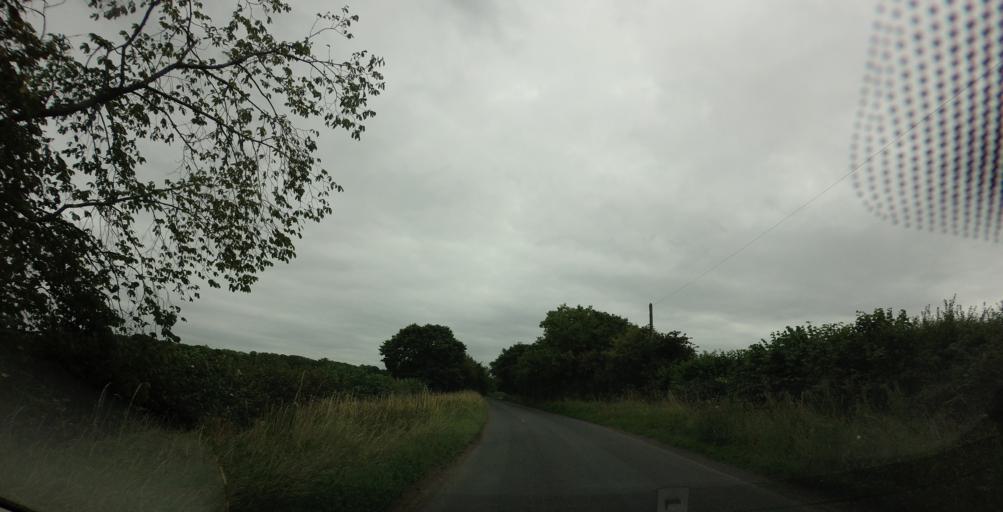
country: GB
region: England
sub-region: North Yorkshire
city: Ripon
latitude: 54.1040
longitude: -1.5168
